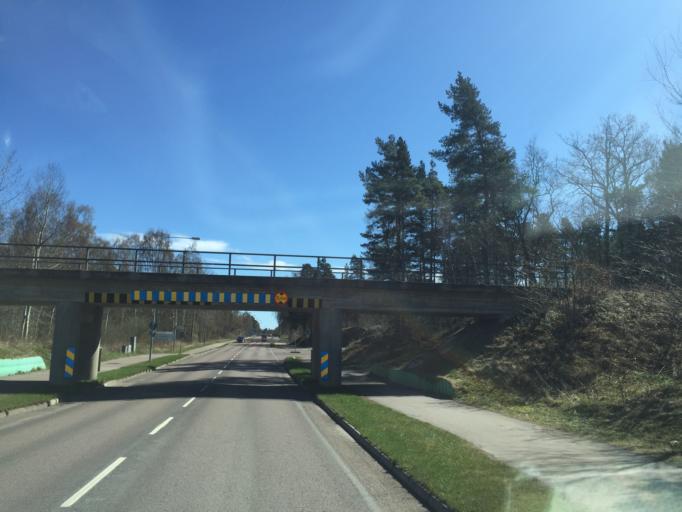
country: SE
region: Kalmar
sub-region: Oskarshamns Kommun
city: Oskarshamn
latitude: 57.2554
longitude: 16.4624
